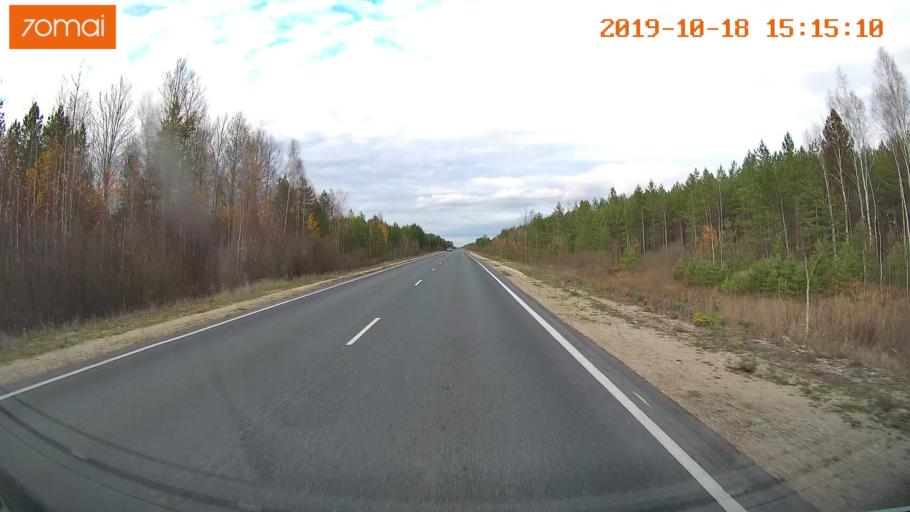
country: RU
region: Vladimir
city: Gus'-Khrustal'nyy
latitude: 55.6144
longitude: 40.7219
